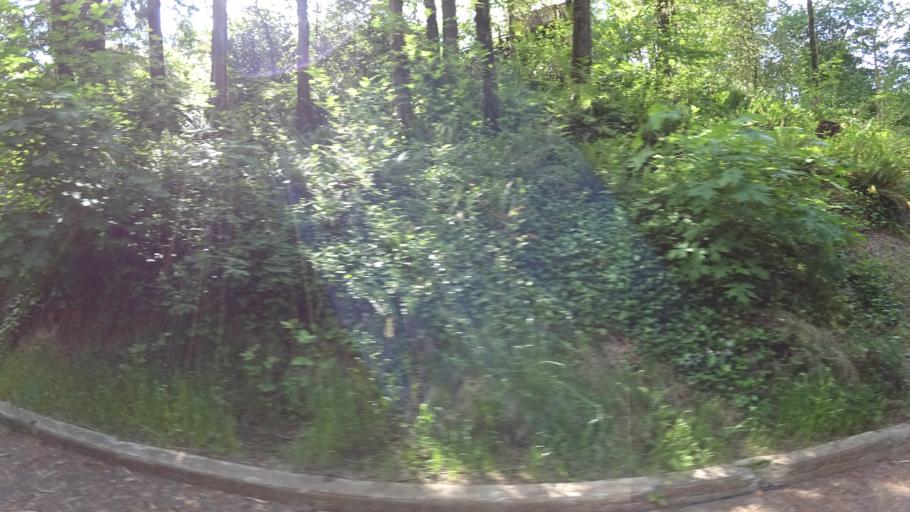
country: US
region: Oregon
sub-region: Multnomah County
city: Portland
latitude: 45.5067
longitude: -122.7081
